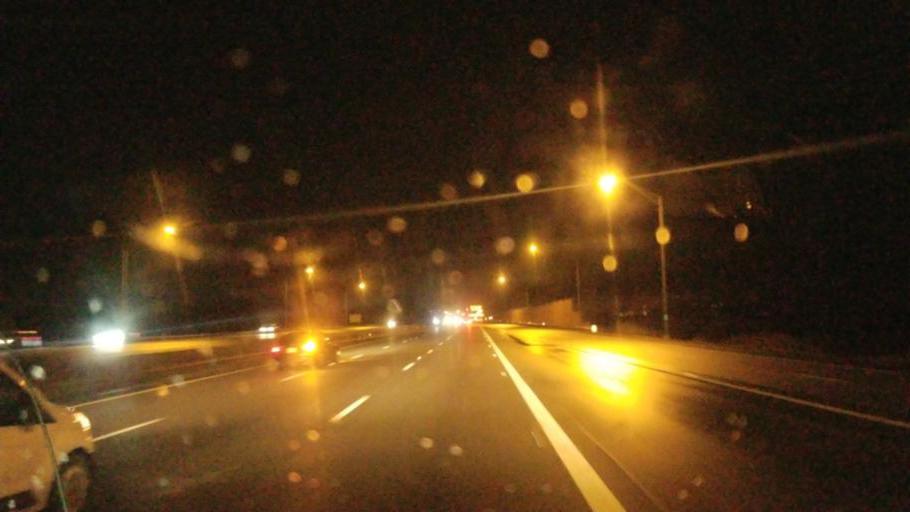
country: US
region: Ohio
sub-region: Medina County
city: Medina
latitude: 41.1391
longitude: -81.7930
